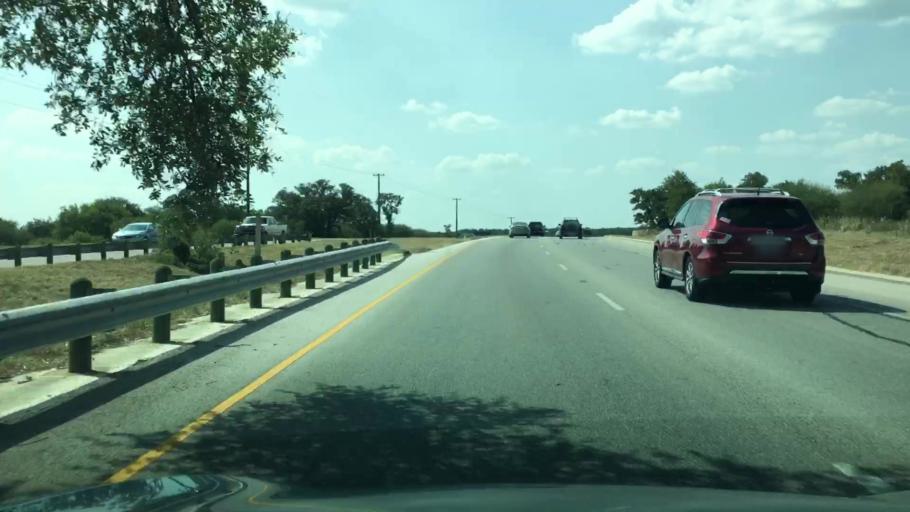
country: US
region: Texas
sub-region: Hays County
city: San Marcos
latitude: 29.8837
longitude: -97.9765
